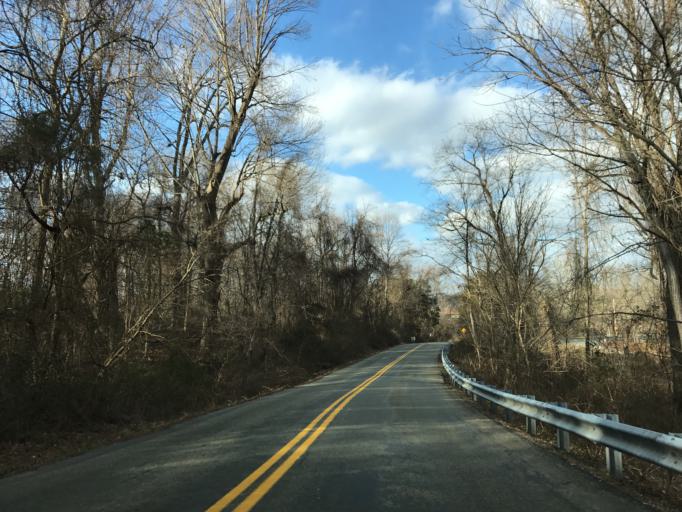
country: US
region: Maryland
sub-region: Cecil County
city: Rising Sun
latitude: 39.6529
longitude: -76.1777
